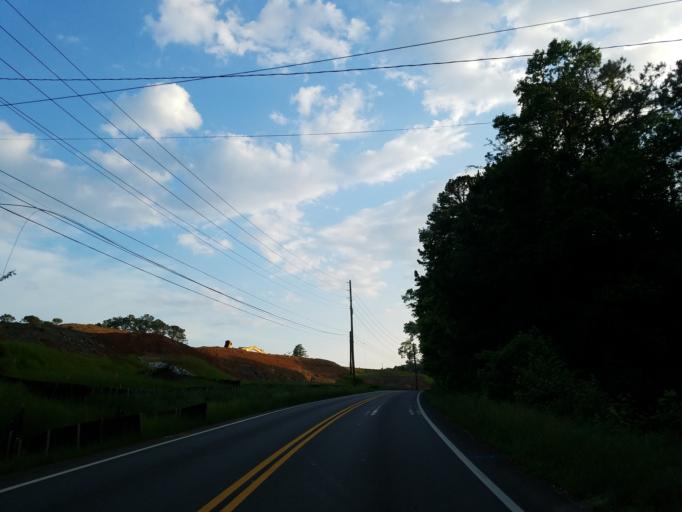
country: US
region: Georgia
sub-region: Cherokee County
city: Holly Springs
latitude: 34.1762
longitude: -84.5530
